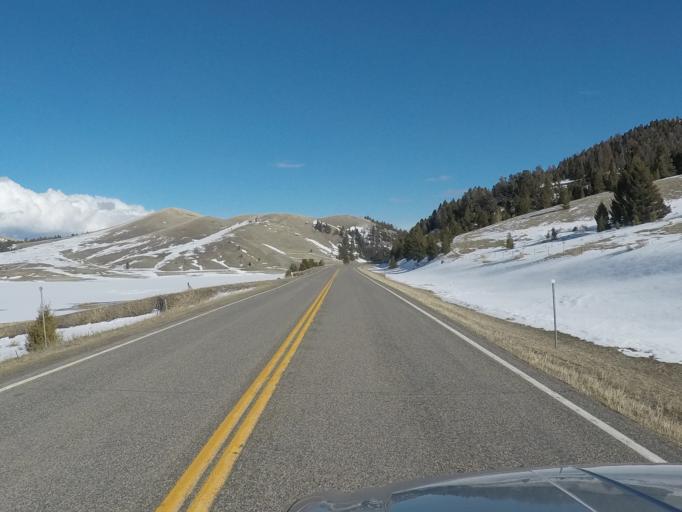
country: US
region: Montana
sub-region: Meagher County
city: White Sulphur Springs
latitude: 46.5812
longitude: -110.5702
